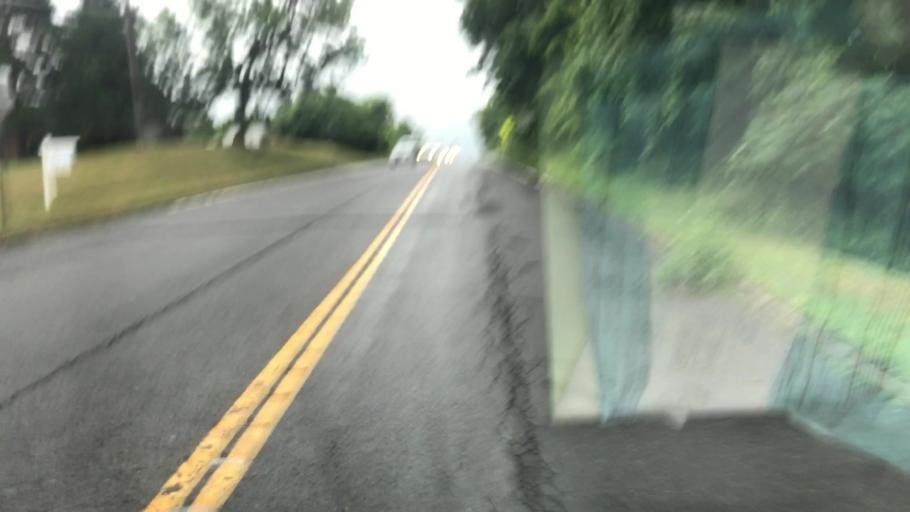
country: US
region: New York
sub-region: Onondaga County
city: Fayetteville
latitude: 43.0269
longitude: -76.0423
